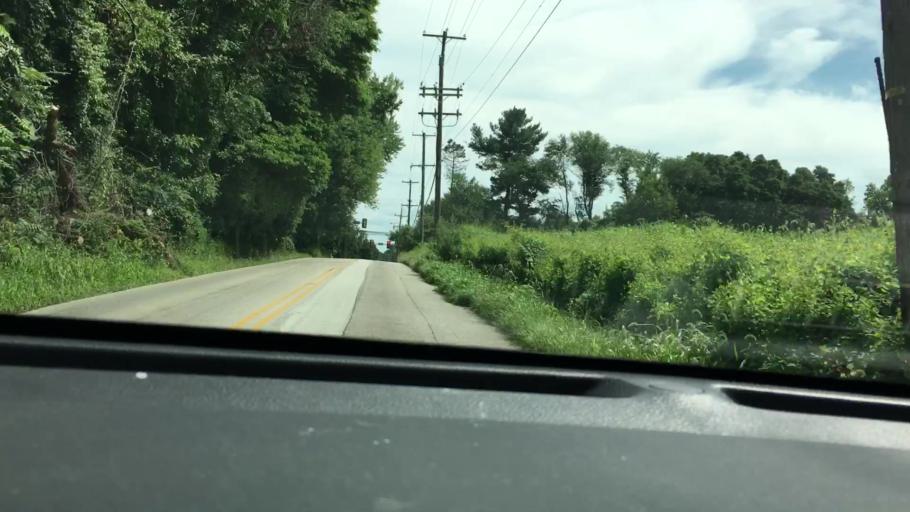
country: US
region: Pennsylvania
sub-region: Montgomery County
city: Bryn Athyn
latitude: 40.1433
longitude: -75.0484
